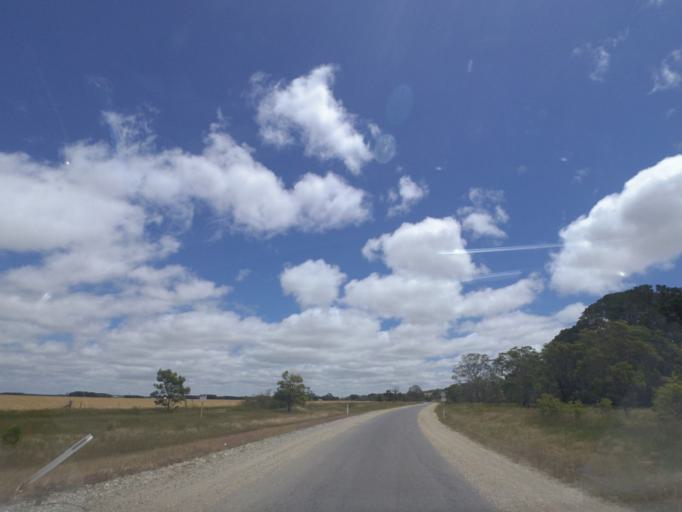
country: AU
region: Victoria
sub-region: Moorabool
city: Bacchus Marsh
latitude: -37.6455
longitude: 144.2911
